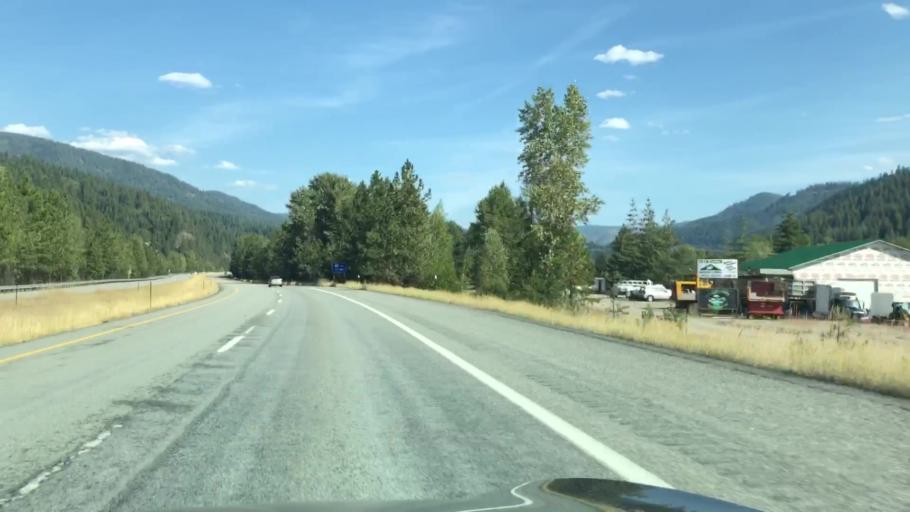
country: US
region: Idaho
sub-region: Shoshone County
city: Osburn
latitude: 47.5091
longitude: -116.0125
